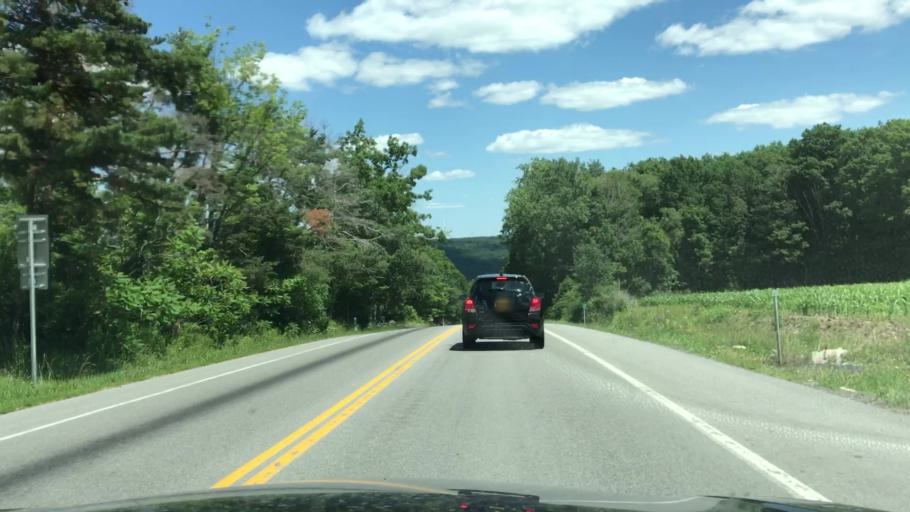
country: US
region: New York
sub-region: Wyoming County
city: Attica
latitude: 42.7704
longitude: -78.3363
